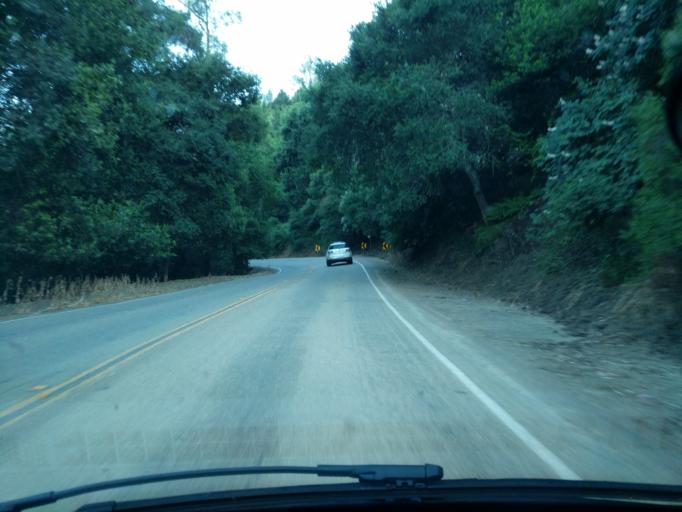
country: US
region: California
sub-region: Alameda County
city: Ashland
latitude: 37.7270
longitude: -122.1174
